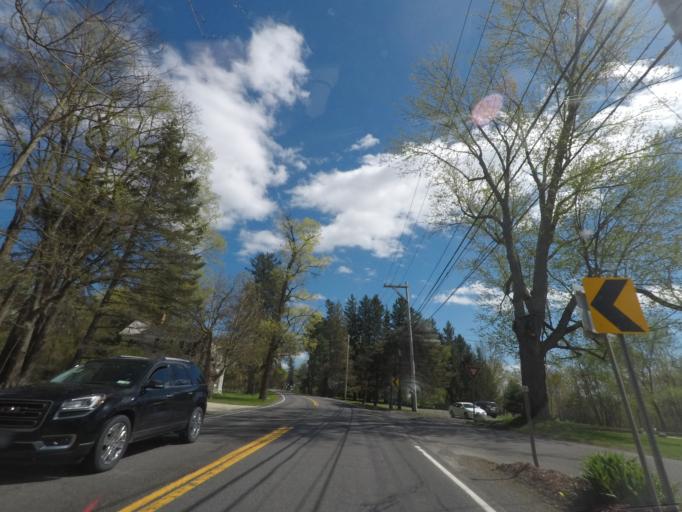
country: US
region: New York
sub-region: Columbia County
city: Oakdale
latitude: 42.2257
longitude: -73.7468
